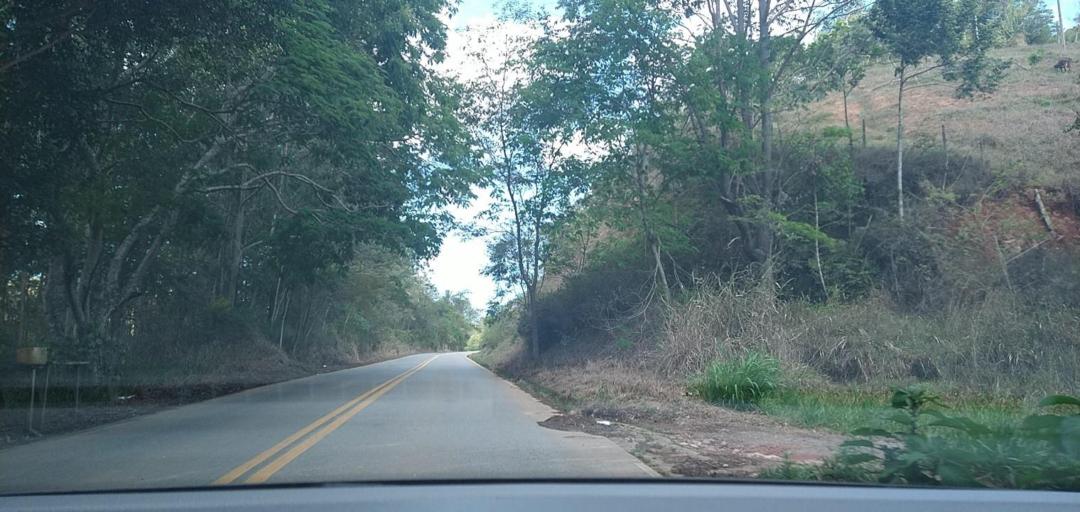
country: BR
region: Minas Gerais
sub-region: Rio Piracicaba
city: Rio Piracicaba
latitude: -20.0015
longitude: -43.1052
